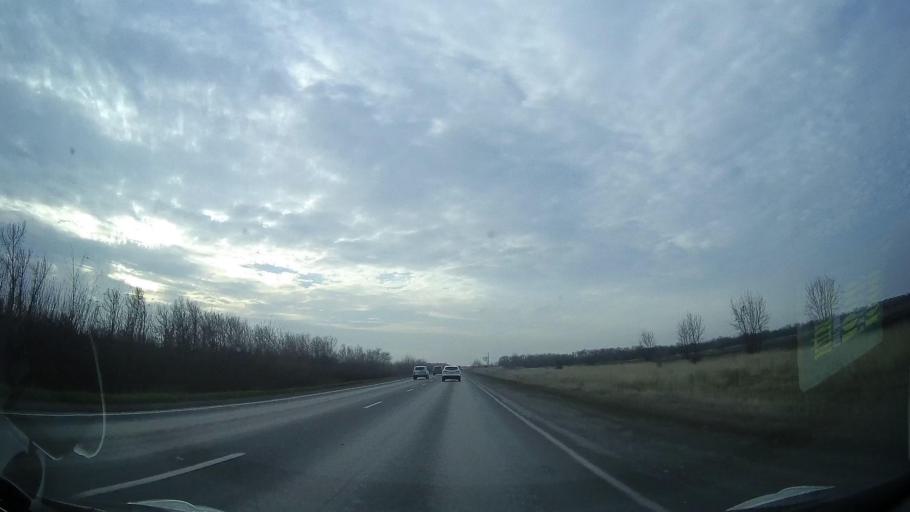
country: RU
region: Rostov
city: Starocherkasskaya
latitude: 47.1402
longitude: 40.0686
